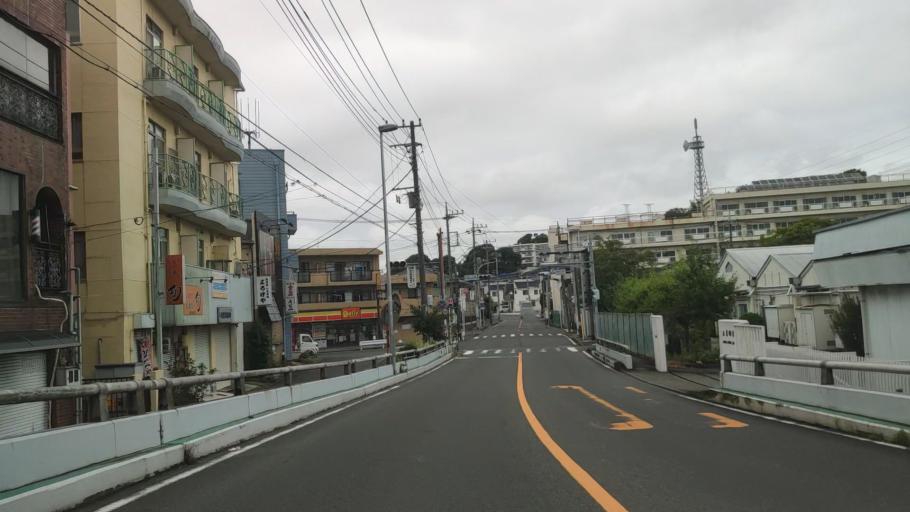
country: JP
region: Kanagawa
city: Yokohama
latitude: 35.4204
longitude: 139.5485
